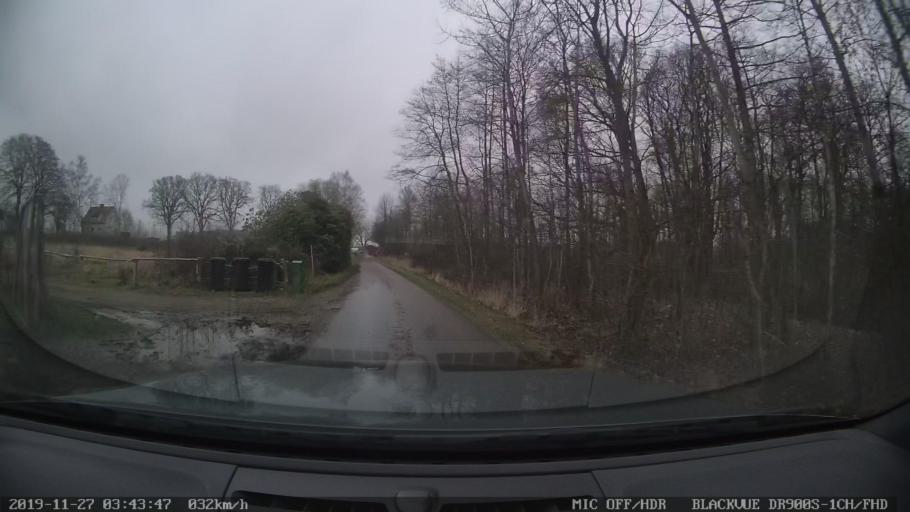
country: SE
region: Skane
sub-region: Hoganas Kommun
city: Hoganas
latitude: 56.2634
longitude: 12.5497
